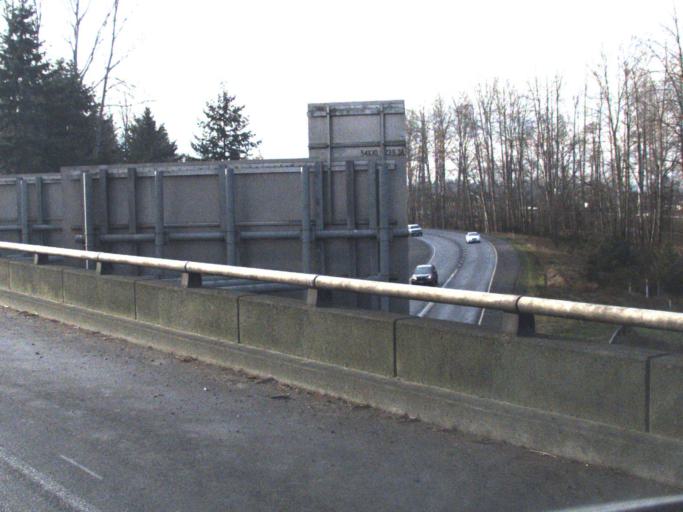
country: US
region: Washington
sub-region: Snohomish County
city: Marysville
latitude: 48.0402
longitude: -122.1793
